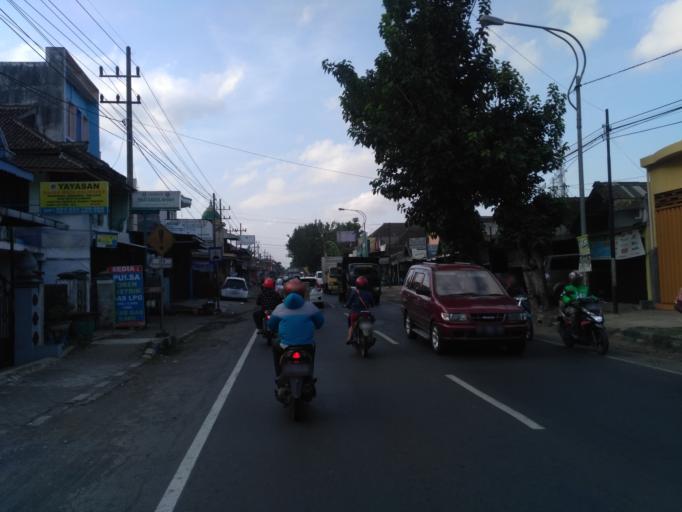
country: ID
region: East Java
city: Pakisaji
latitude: -8.0663
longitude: 112.5985
